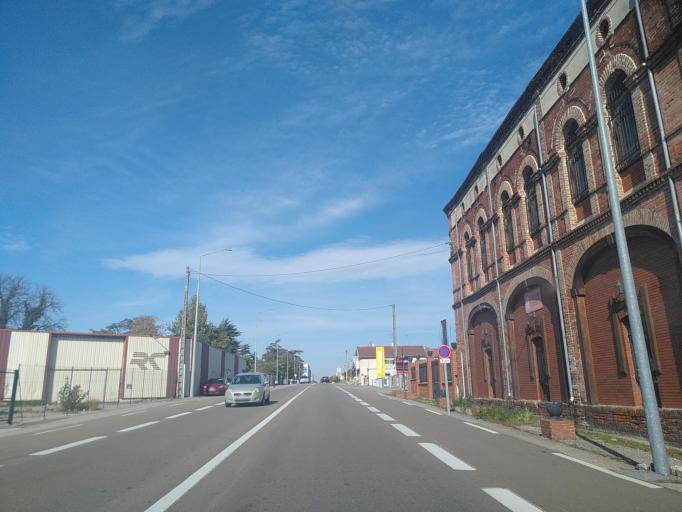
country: FR
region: Rhone-Alpes
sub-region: Departement de la Drome
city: Saint-Vallier
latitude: 45.1892
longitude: 4.8141
